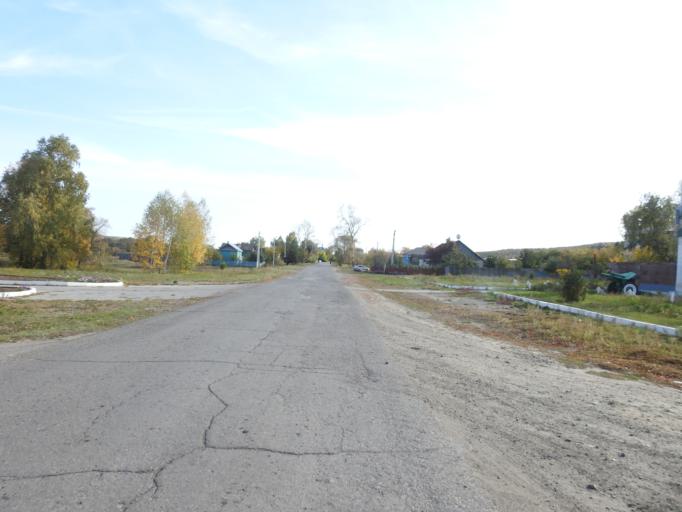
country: RU
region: Saratov
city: Baltay
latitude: 52.5088
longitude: 46.8013
